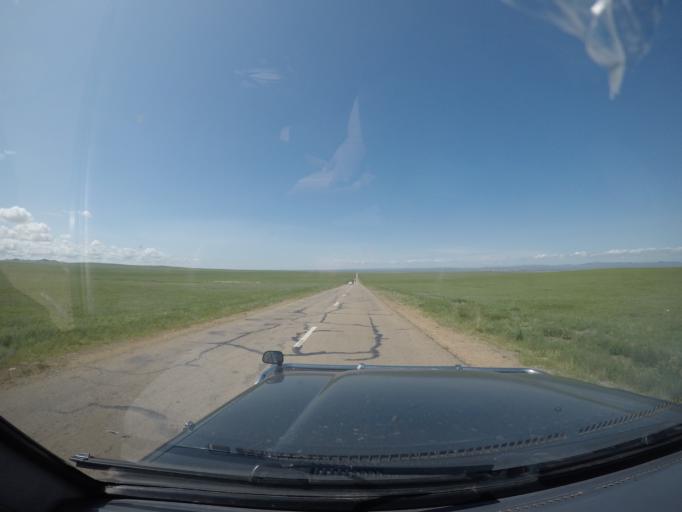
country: MN
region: Hentiy
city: Bayan
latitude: 47.2799
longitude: 110.8308
